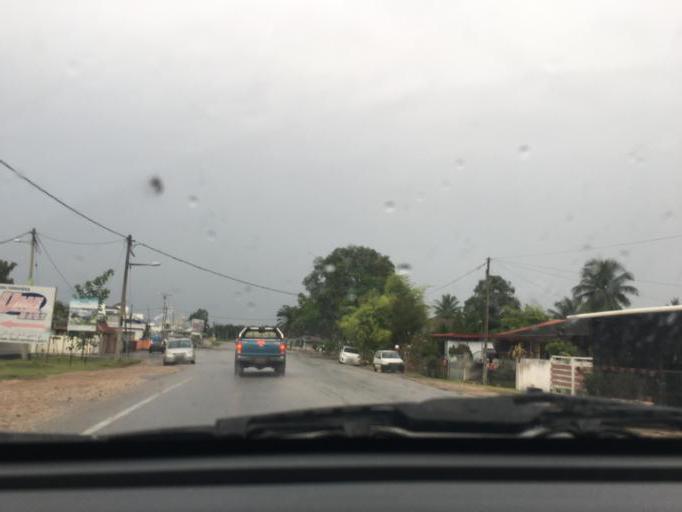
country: MY
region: Kedah
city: Sungai Petani
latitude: 5.6093
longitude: 100.6397
